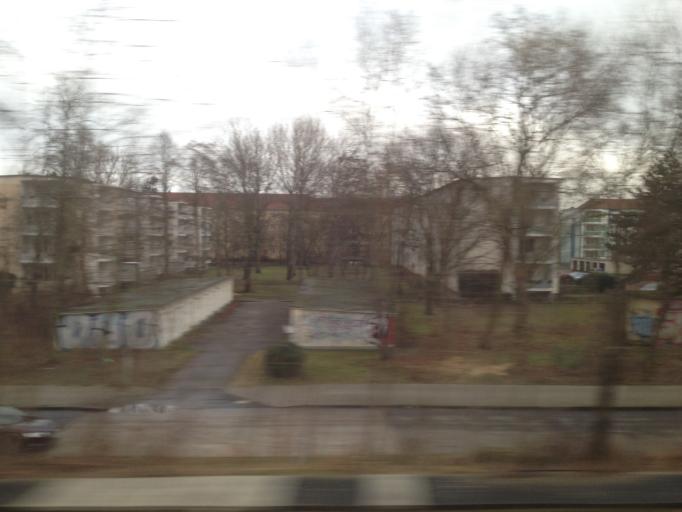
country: DE
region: Berlin
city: Plaenterwald
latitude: 52.4743
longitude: 13.4794
